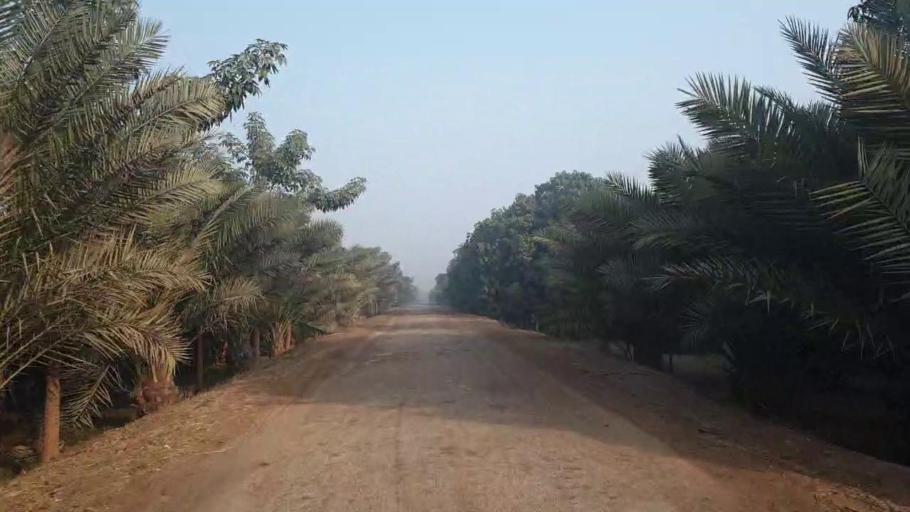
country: PK
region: Sindh
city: Tando Adam
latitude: 25.7881
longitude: 68.6403
